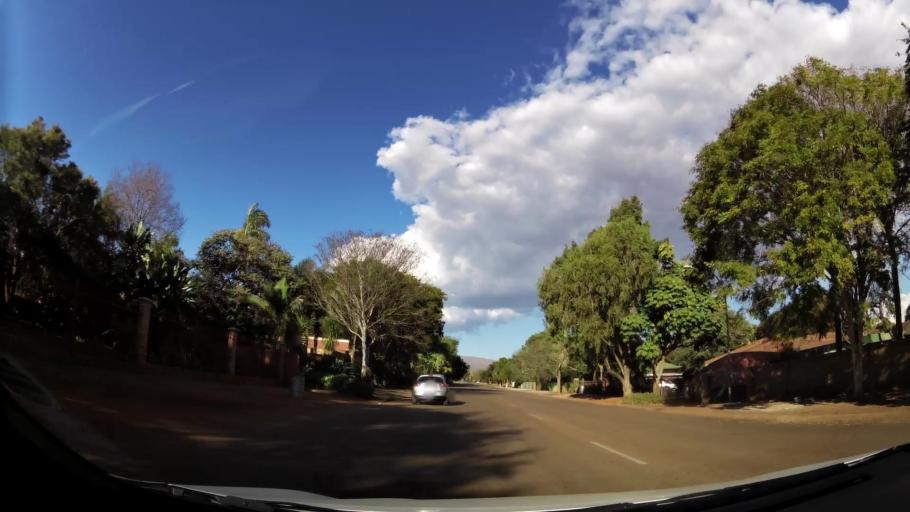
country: ZA
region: Limpopo
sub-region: Waterberg District Municipality
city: Mokopane
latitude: -24.2039
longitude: 29.0030
